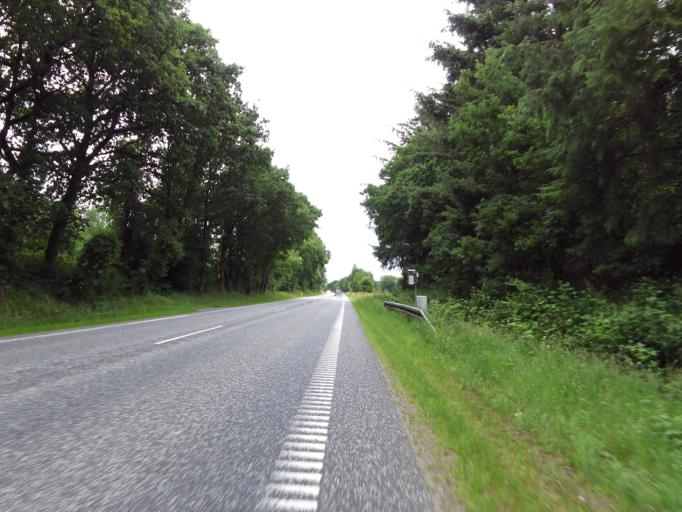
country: DK
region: South Denmark
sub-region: Tonder Kommune
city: Logumkloster
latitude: 55.0985
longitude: 8.9404
